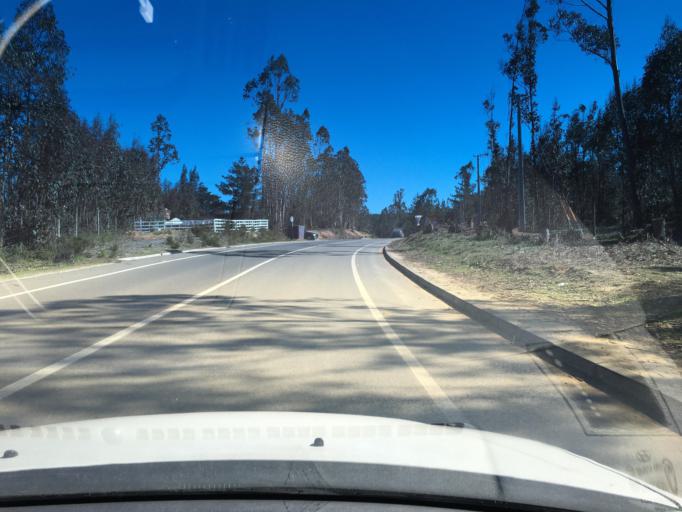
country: CL
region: Valparaiso
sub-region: San Antonio Province
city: El Tabo
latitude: -33.4248
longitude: -71.6333
